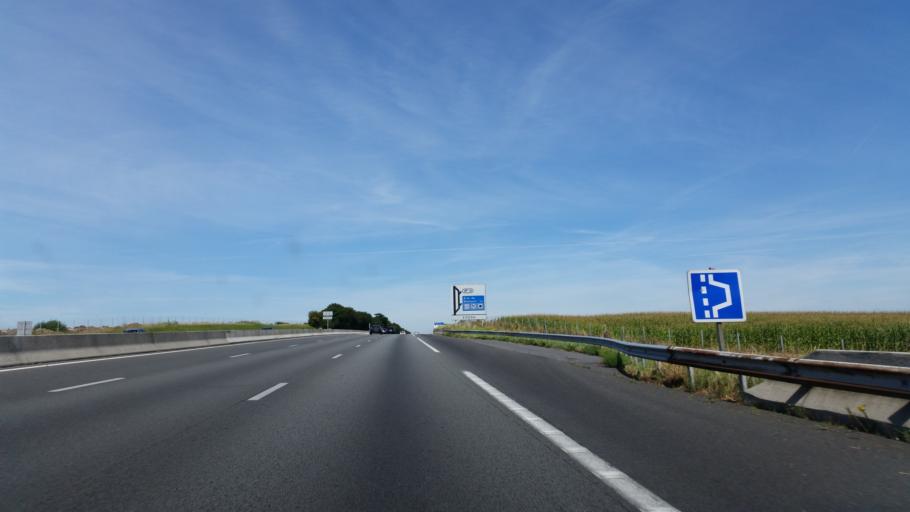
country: FR
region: Nord-Pas-de-Calais
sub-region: Departement du Pas-de-Calais
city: Croisilles
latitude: 50.2393
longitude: 2.8549
